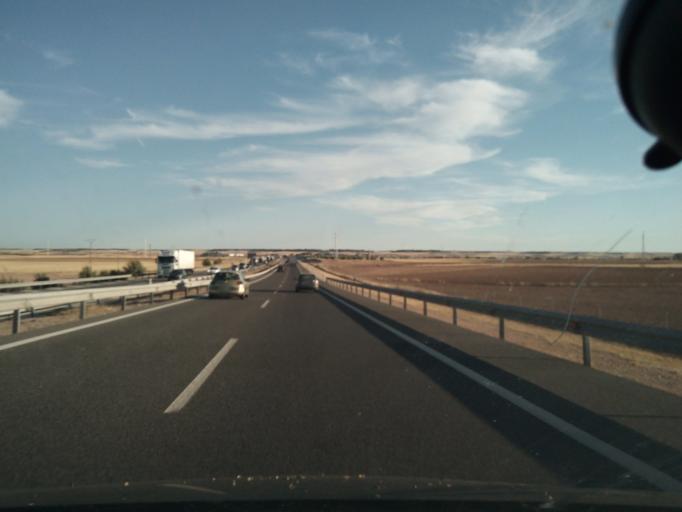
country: ES
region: Castille-La Mancha
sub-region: Province of Toledo
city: Tembleque
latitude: 39.7171
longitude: -3.4946
